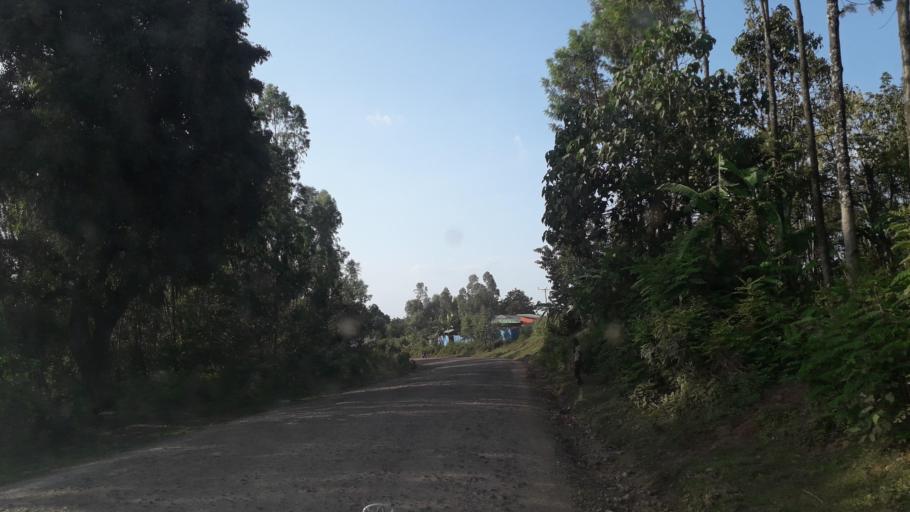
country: ET
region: Oromiya
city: Jima
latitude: 7.5444
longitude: 36.8755
